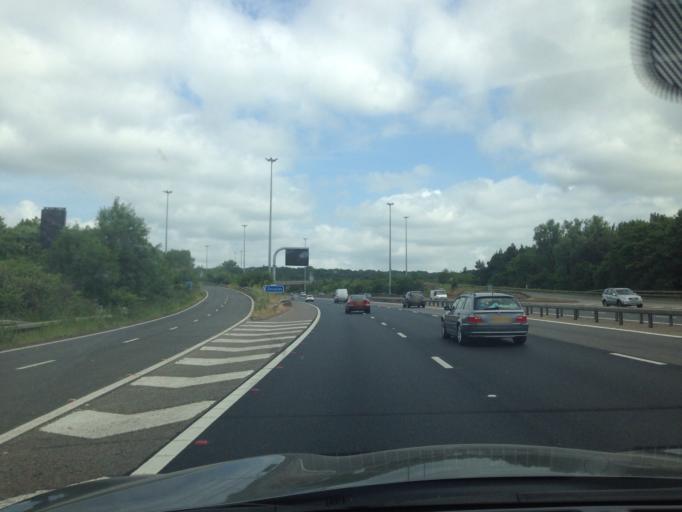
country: GB
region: England
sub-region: Greater London
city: Edgware
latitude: 51.6315
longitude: -0.2632
